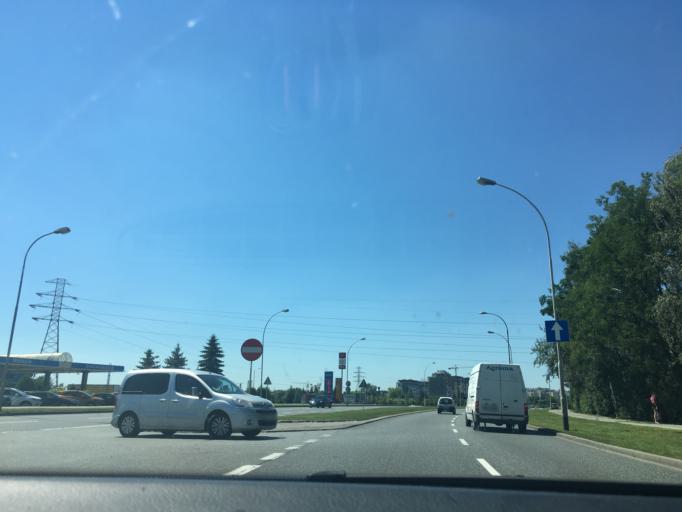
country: PL
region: Subcarpathian Voivodeship
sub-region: Rzeszow
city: Rzeszow
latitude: 50.0183
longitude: 22.0246
